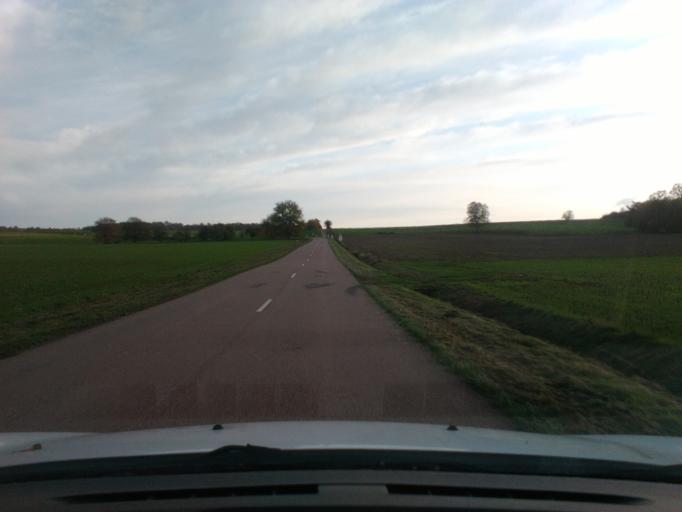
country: FR
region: Lorraine
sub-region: Departement des Vosges
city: Mirecourt
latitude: 48.2276
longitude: 6.1492
